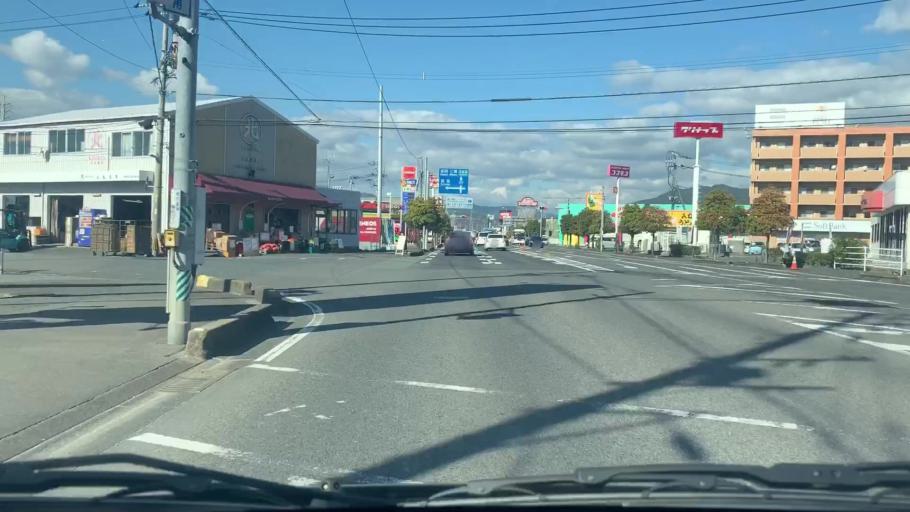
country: JP
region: Saga Prefecture
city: Saga-shi
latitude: 33.2906
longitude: 130.2867
